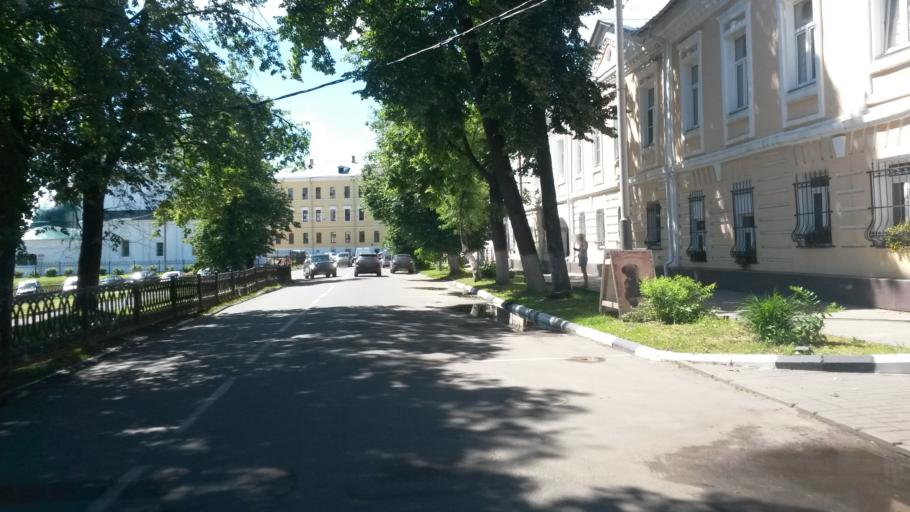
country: RU
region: Jaroslavl
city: Yaroslavl
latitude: 57.6235
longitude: 39.8971
